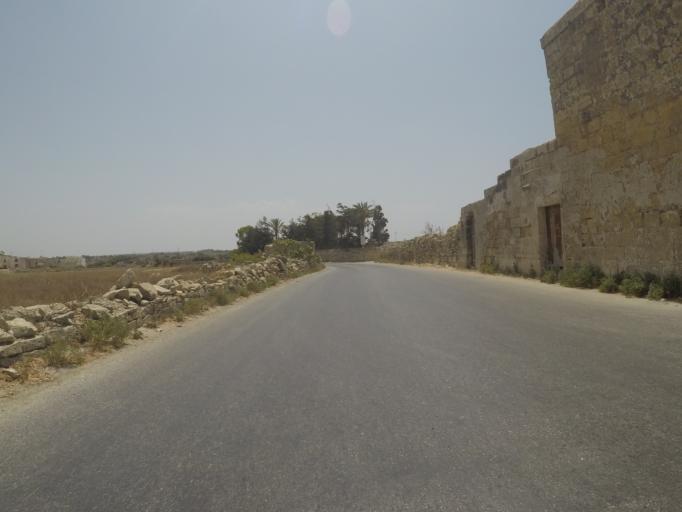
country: MT
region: Is-Siggiewi
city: Siggiewi
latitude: 35.8521
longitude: 14.4310
